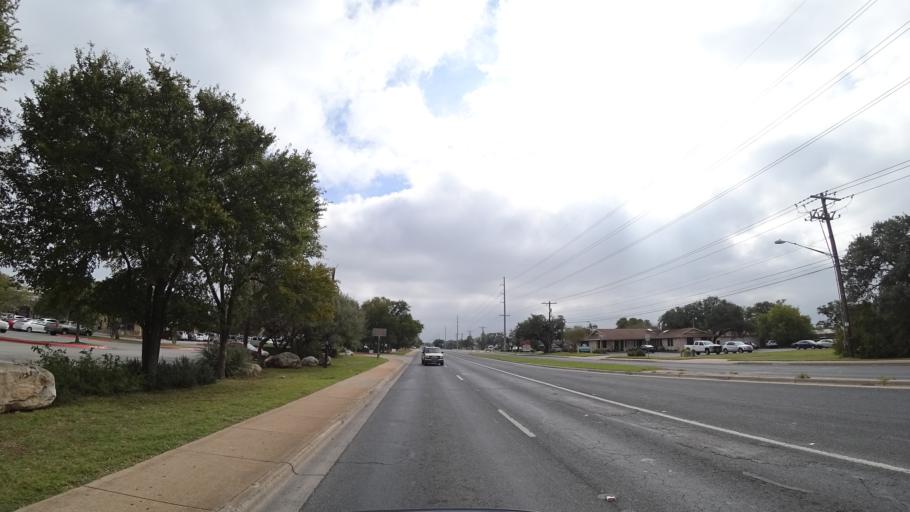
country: US
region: Texas
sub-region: Travis County
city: Shady Hollow
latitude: 30.1833
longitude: -97.8492
